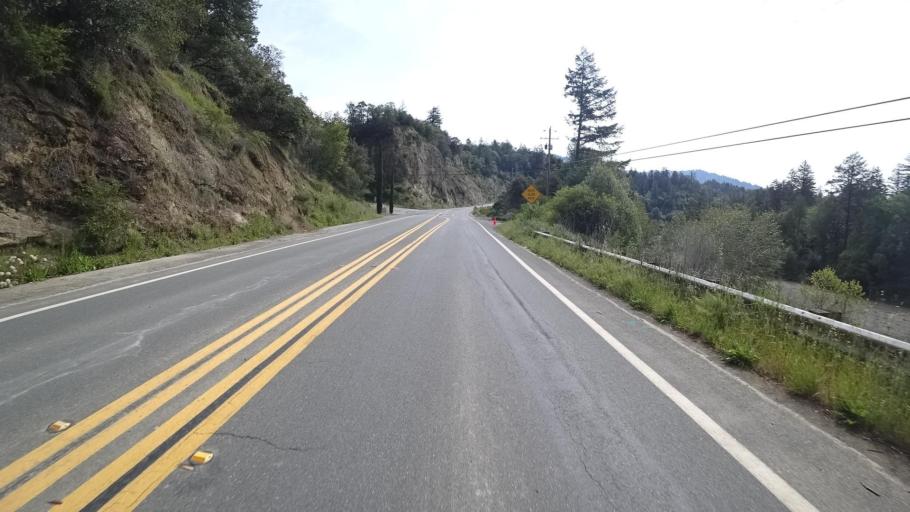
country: US
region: California
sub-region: Humboldt County
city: Redway
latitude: 40.1167
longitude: -123.8015
